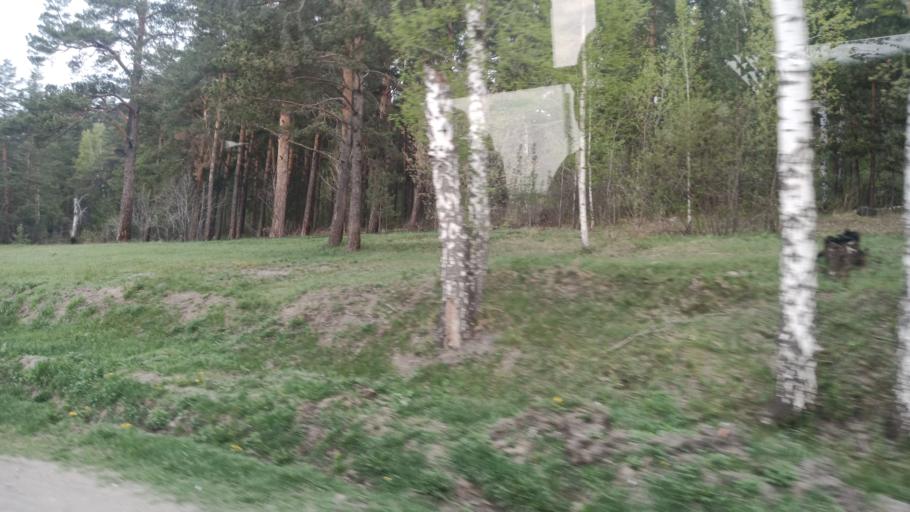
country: RU
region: Altai Krai
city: Yuzhnyy
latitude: 53.2668
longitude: 83.7192
